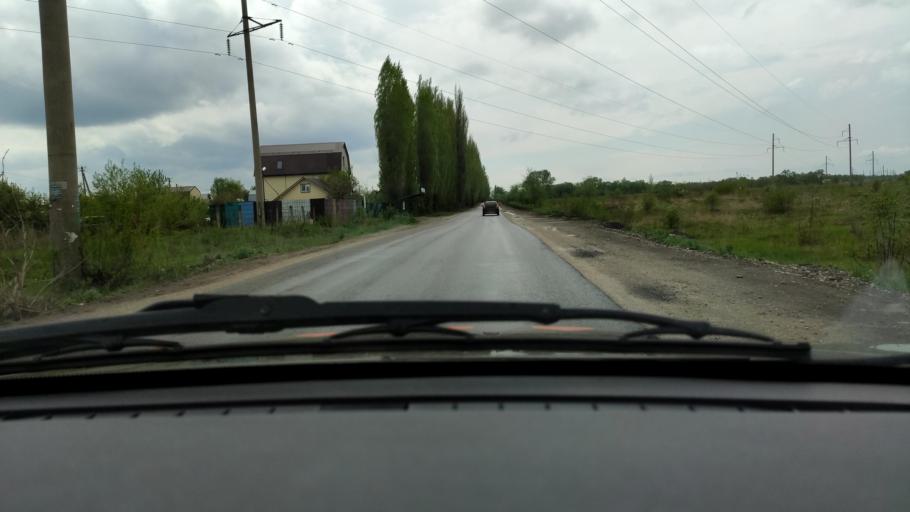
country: RU
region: Voronezj
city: Maslovka
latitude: 51.5241
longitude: 39.2273
